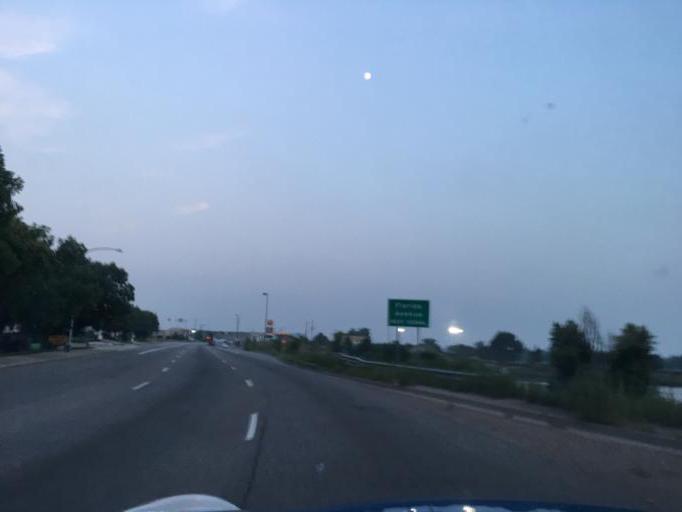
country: US
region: Colorado
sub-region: Arapahoe County
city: Englewood
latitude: 39.6922
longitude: -104.9944
